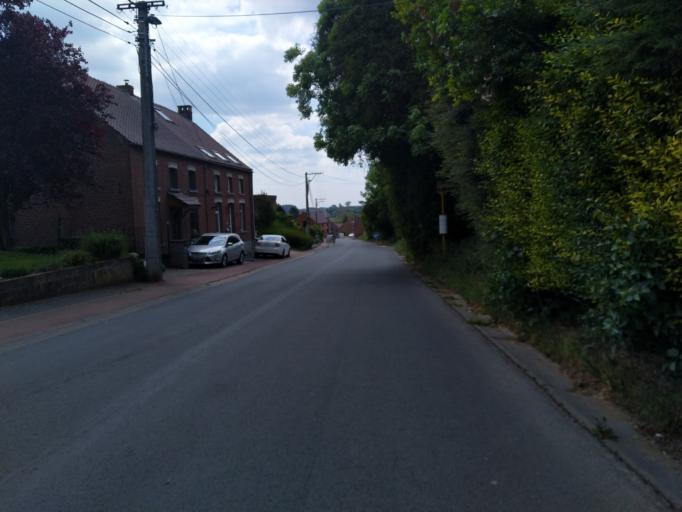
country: BE
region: Wallonia
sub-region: Province du Hainaut
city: Enghien
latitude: 50.6369
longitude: 3.9972
